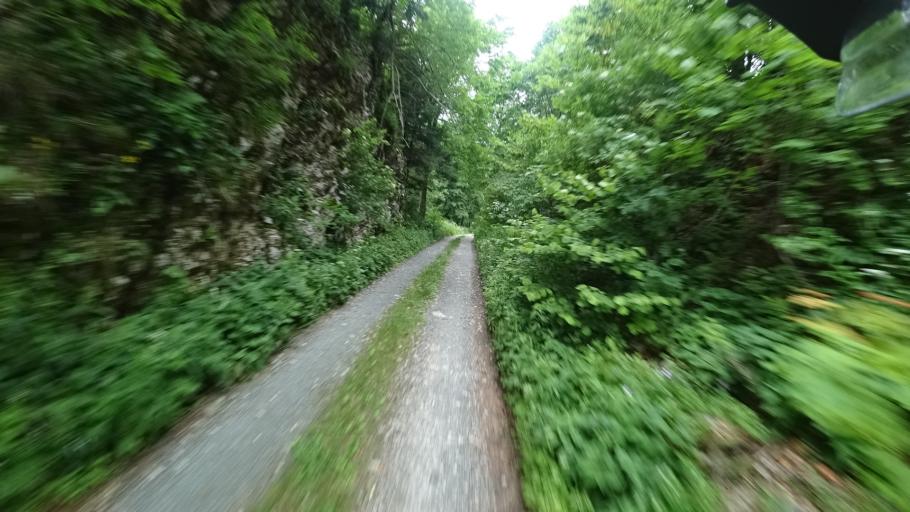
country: HR
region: Primorsko-Goranska
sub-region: Grad Crikvenica
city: Crikvenica
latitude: 45.2625
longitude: 14.7064
